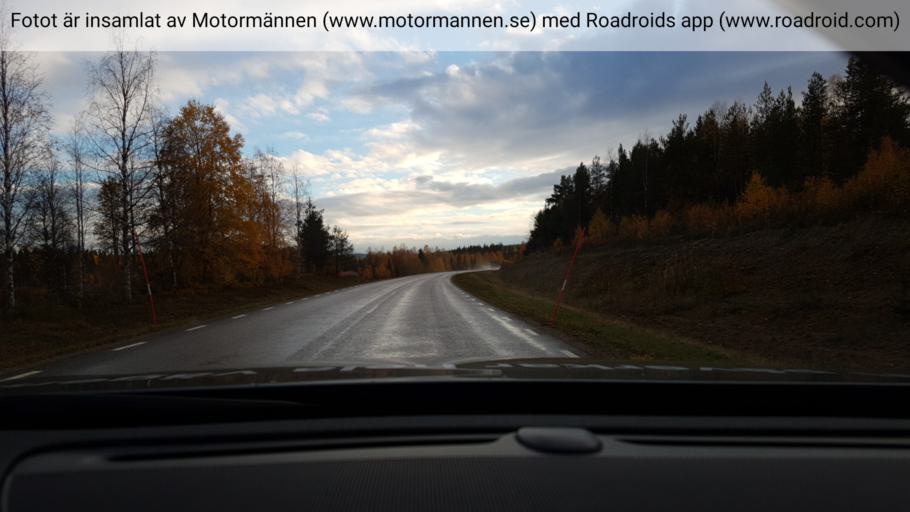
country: SE
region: Norrbotten
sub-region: Overkalix Kommun
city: OEverkalix
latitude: 66.7635
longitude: 22.6828
